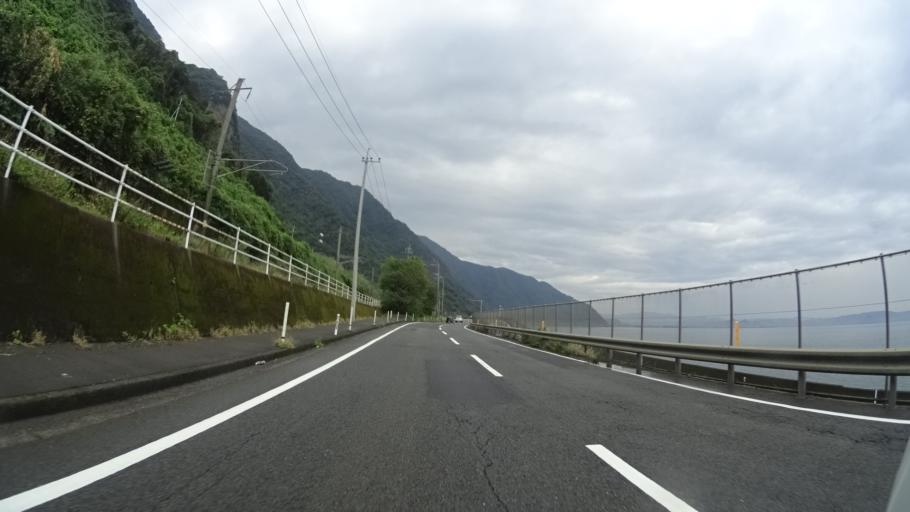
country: JP
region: Kagoshima
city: Kajiki
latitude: 31.6623
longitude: 130.6148
